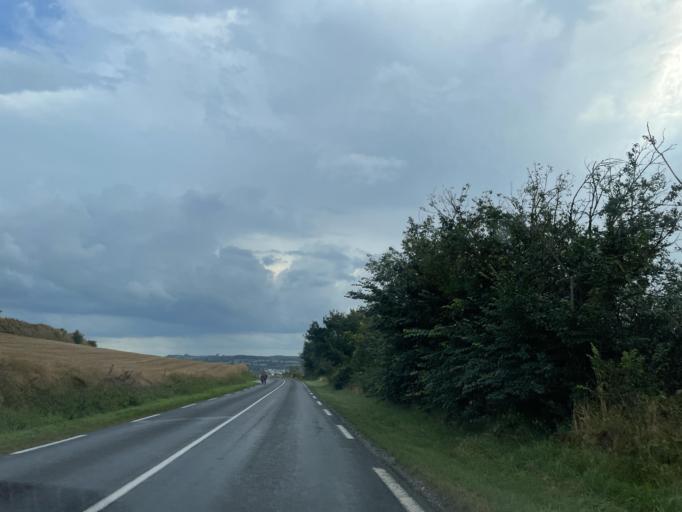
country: FR
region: Haute-Normandie
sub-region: Departement de la Seine-Maritime
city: Neufchatel-en-Bray
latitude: 49.7467
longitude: 1.4318
